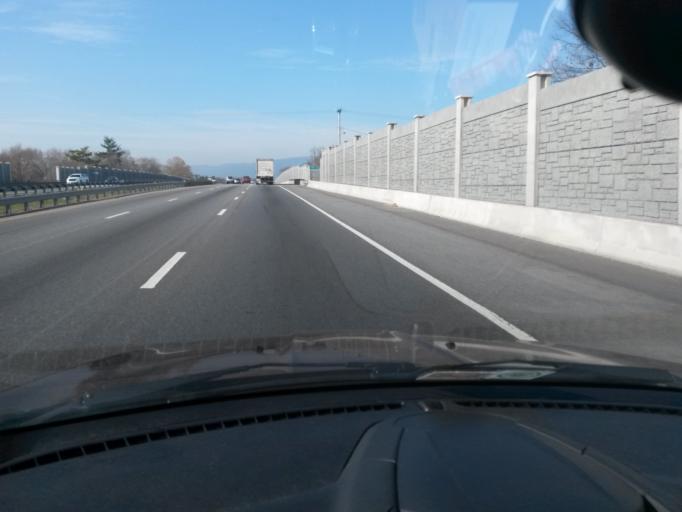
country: US
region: Virginia
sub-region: City of Roanoke
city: Roanoke
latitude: 37.2934
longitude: -79.9476
